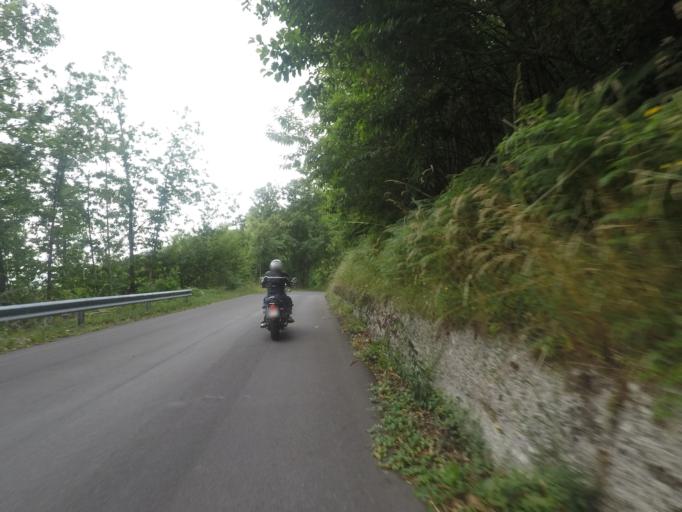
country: IT
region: Tuscany
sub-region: Provincia di Lucca
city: Careggine
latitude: 44.1154
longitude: 10.3616
